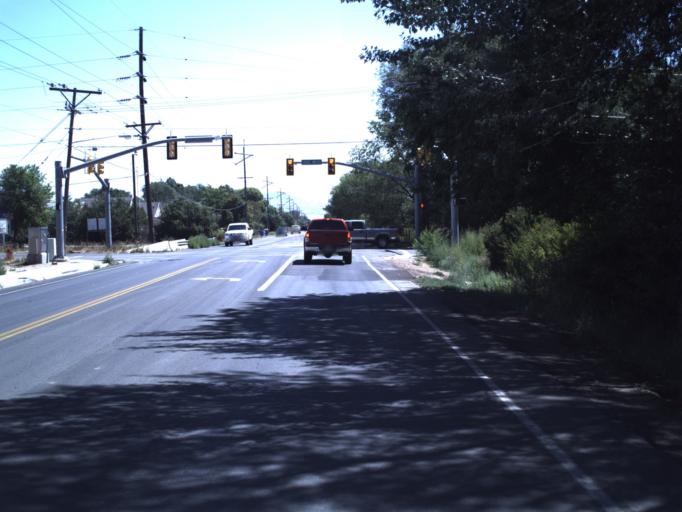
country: US
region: Utah
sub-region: Uintah County
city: Vernal
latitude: 40.4627
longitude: -109.5581
